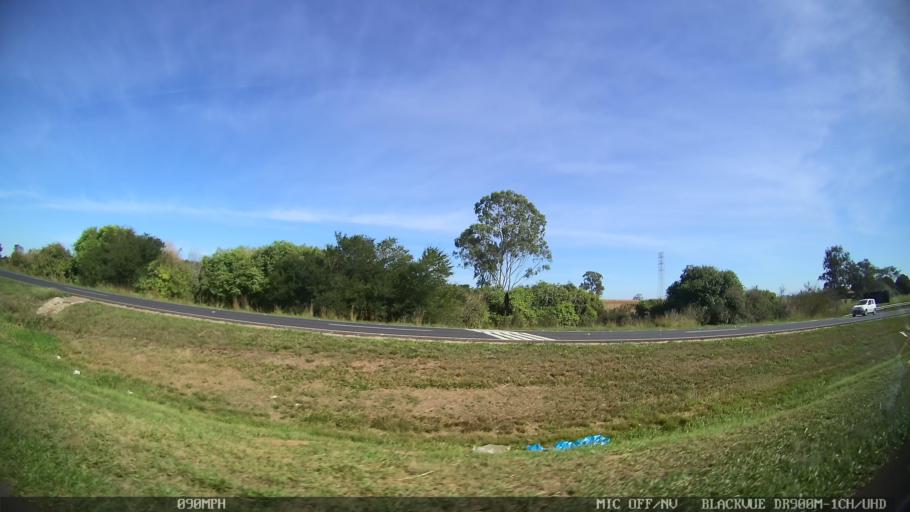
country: BR
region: Sao Paulo
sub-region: Pirassununga
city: Pirassununga
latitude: -22.0596
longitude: -47.4269
